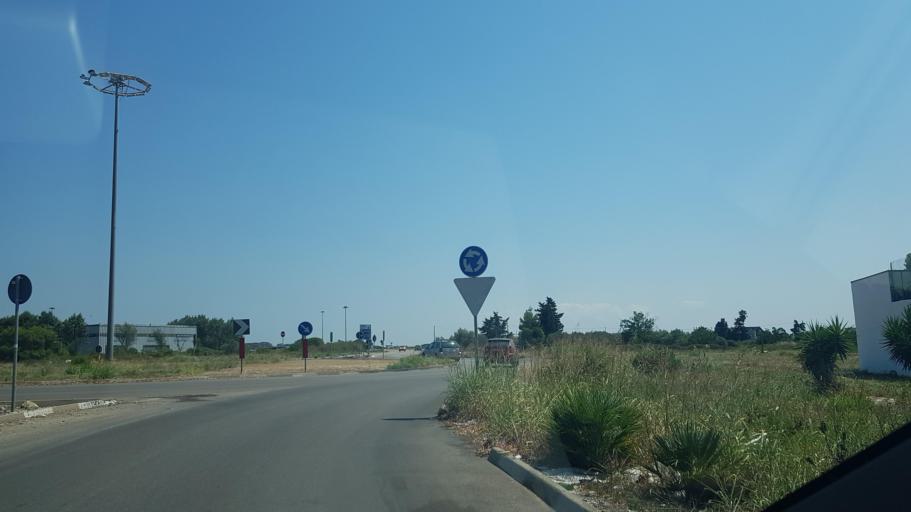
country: IT
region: Apulia
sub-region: Provincia di Lecce
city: Merine
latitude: 40.3454
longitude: 18.1998
